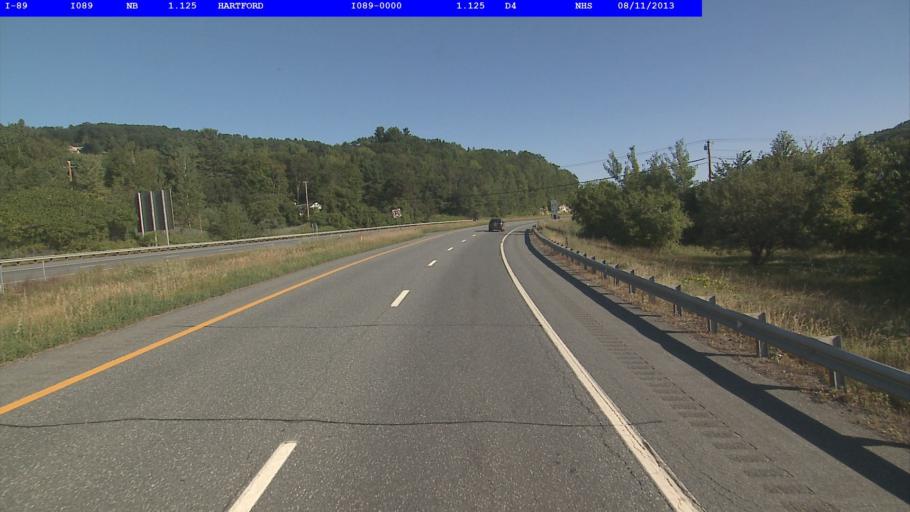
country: US
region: Vermont
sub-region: Windsor County
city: White River Junction
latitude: 43.6457
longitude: -72.3462
